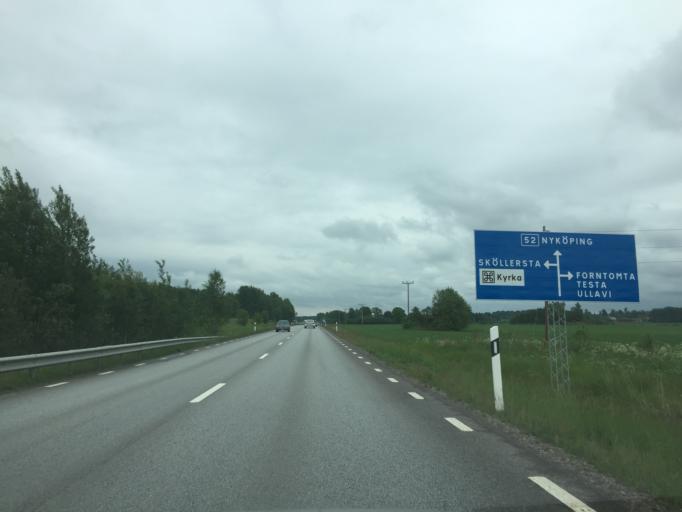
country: SE
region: OErebro
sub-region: Hallsbergs Kommun
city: Skollersta
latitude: 59.1345
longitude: 15.3458
